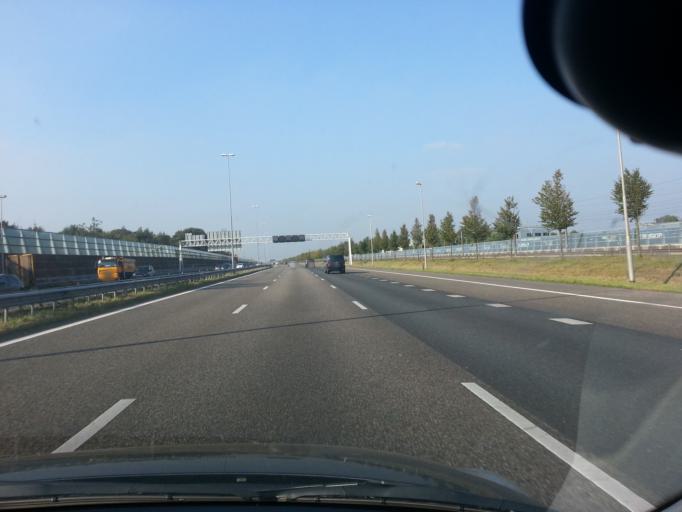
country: NL
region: North Brabant
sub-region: Gemeente Breda
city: Breda
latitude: 51.6069
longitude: 4.7194
